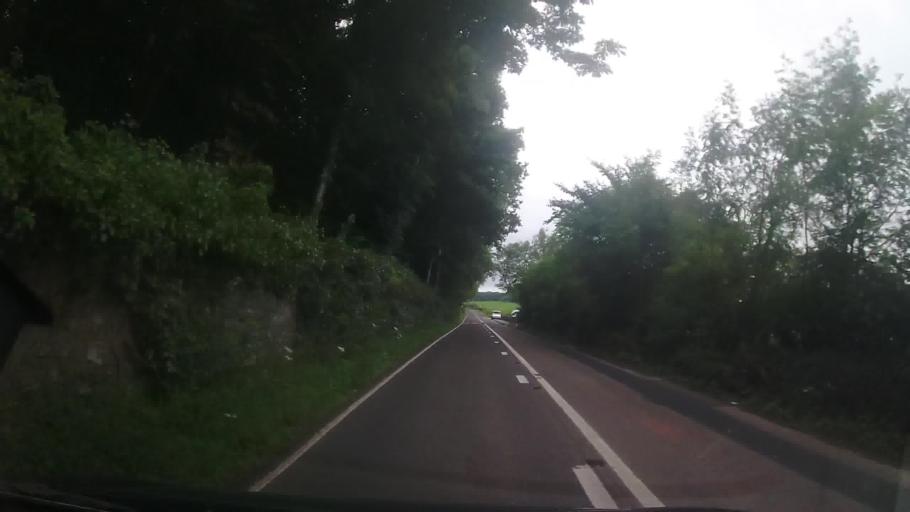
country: GB
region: Wales
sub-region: Anglesey
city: Llanfairpwllgwyngyll
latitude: 53.2158
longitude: -4.2098
